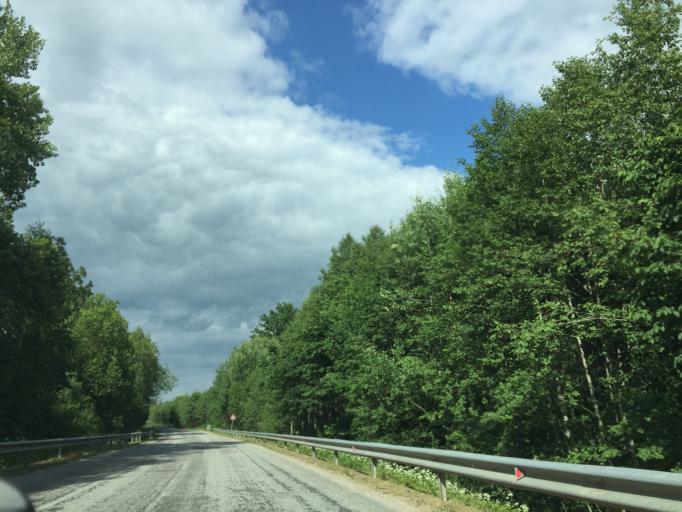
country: LV
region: Skriveri
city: Skriveri
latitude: 56.8075
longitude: 25.1102
